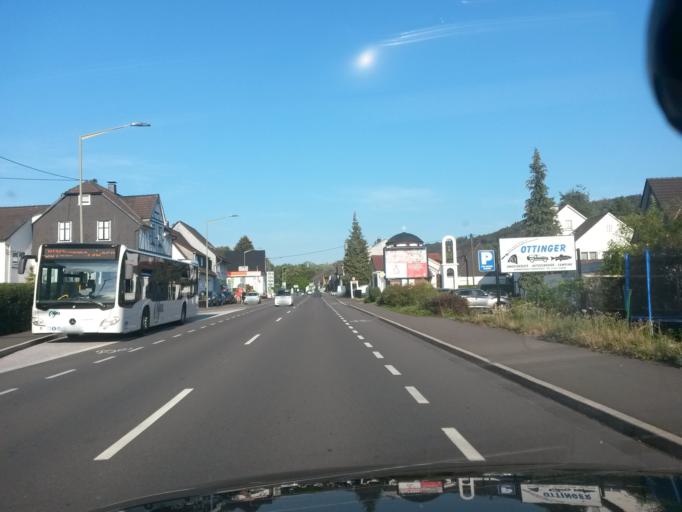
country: DE
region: North Rhine-Westphalia
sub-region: Regierungsbezirk Koln
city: Gummersbach
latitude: 51.0041
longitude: 7.5940
